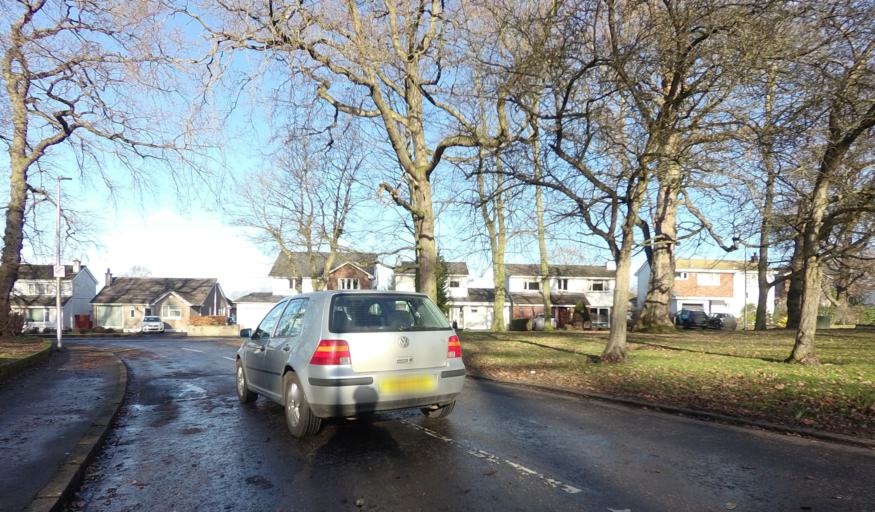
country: GB
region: Scotland
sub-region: Edinburgh
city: Colinton
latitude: 55.9615
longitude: -3.2933
